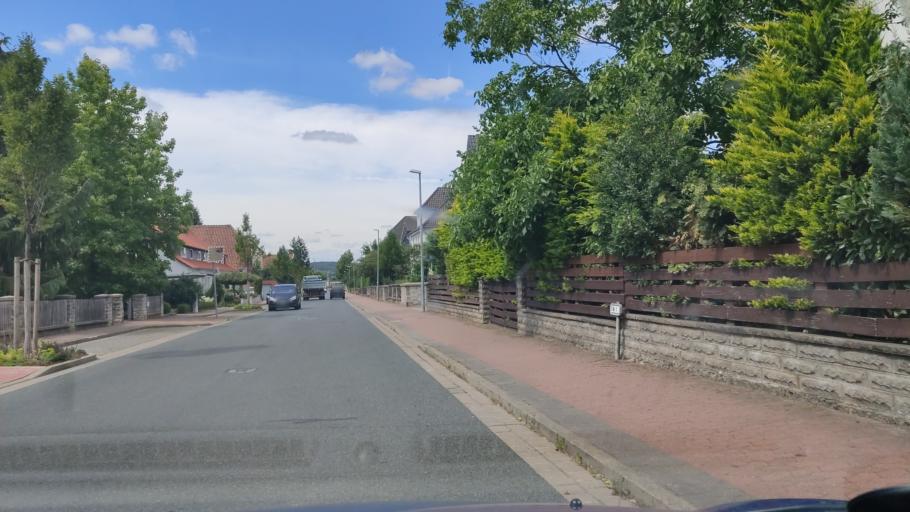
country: DE
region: Lower Saxony
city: Ronnenberg
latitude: 52.3198
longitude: 9.6528
